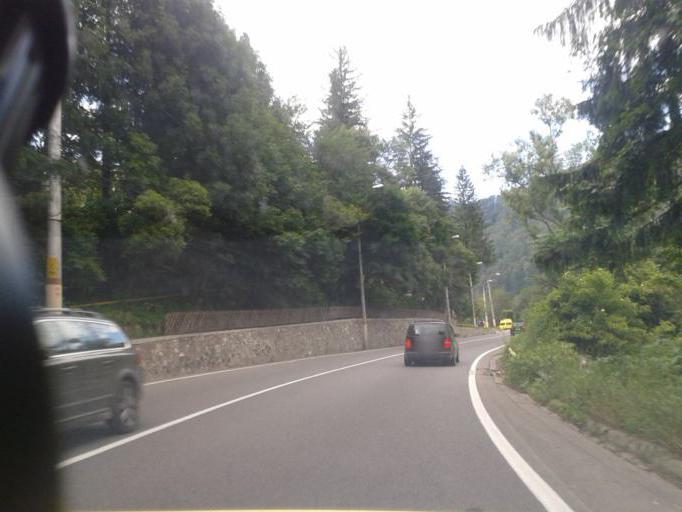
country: RO
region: Prahova
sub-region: Oras Sinaia
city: Sinaia
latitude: 45.3221
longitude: 25.5635
